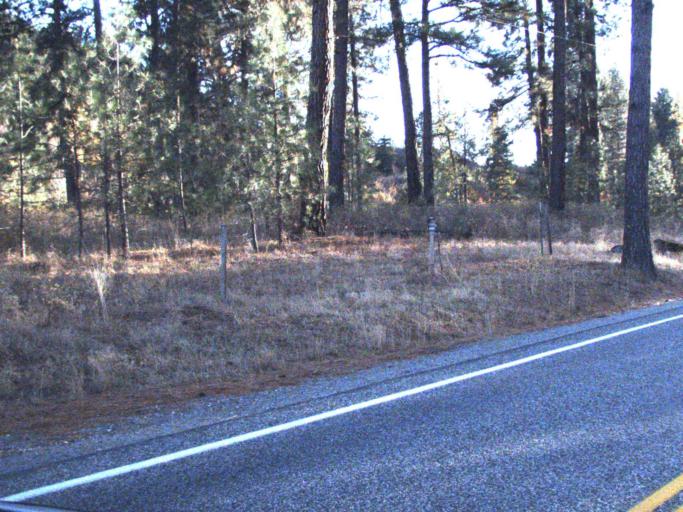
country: US
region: Washington
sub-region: Stevens County
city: Kettle Falls
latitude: 48.7602
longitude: -118.0376
